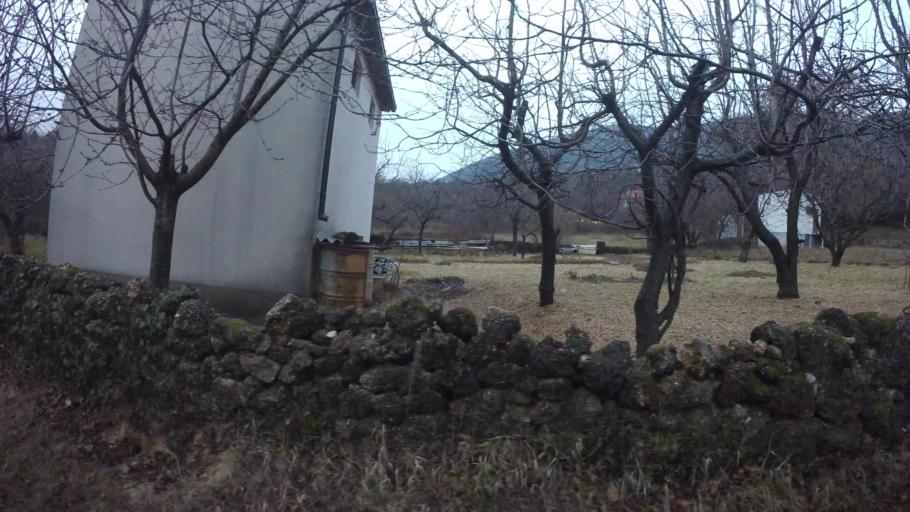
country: BA
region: Federation of Bosnia and Herzegovina
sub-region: Hercegovacko-Bosanski Kanton
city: Mostar
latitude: 43.3660
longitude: 17.8030
